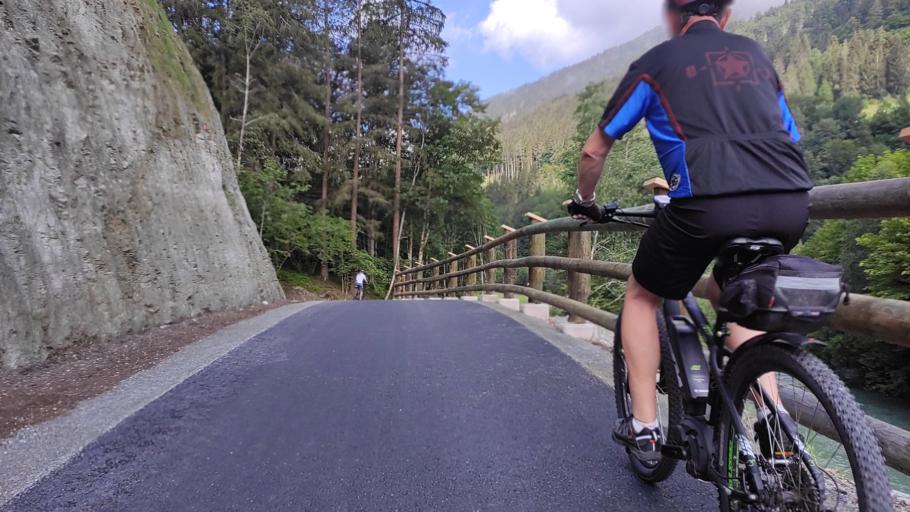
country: AT
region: Salzburg
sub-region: Politischer Bezirk Zell am See
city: Maishofen
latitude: 47.3651
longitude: 12.7747
